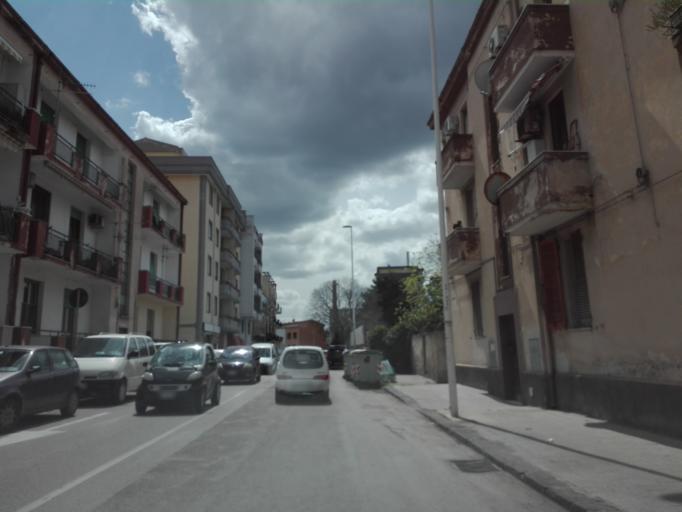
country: IT
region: Sardinia
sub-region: Provincia di Sassari
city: Sassari
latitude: 40.7347
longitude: 8.5565
